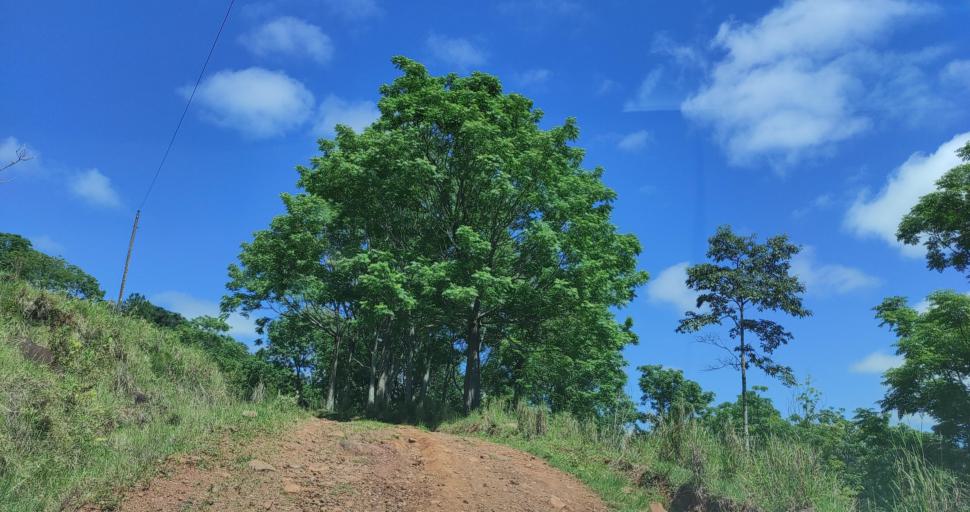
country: AR
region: Misiones
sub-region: Departamento de Veinticinco de Mayo
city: Veinticinco de Mayo
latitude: -27.4162
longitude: -54.7194
